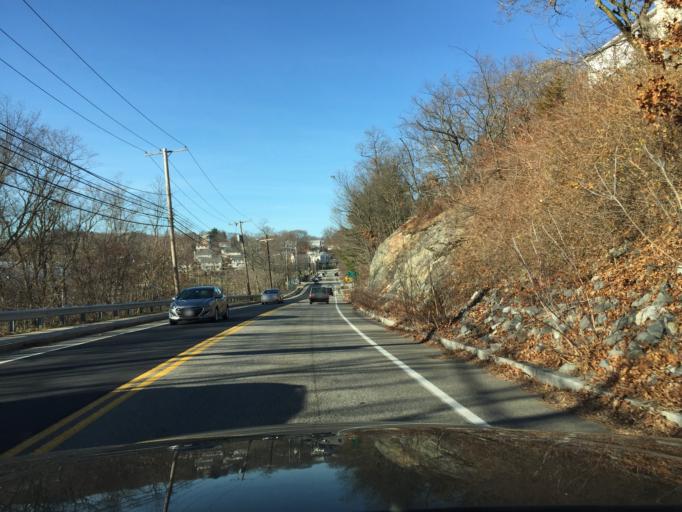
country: US
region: Massachusetts
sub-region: Middlesex County
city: Arlington
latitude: 42.4250
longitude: -71.1710
